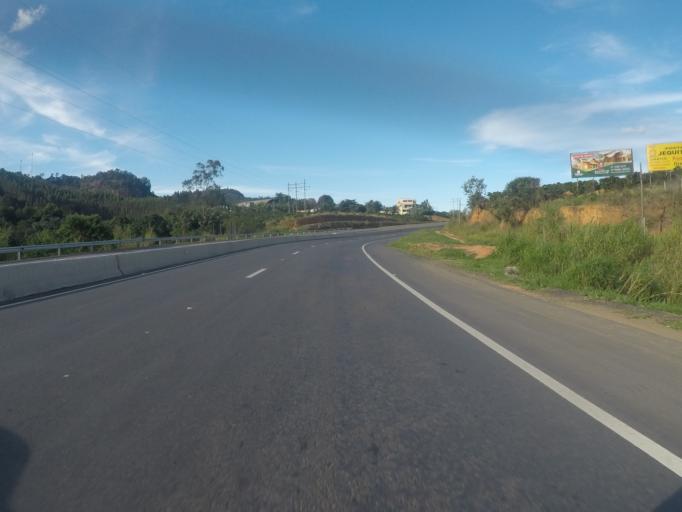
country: BR
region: Espirito Santo
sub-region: Ibiracu
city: Ibiracu
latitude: -19.8641
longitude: -40.3924
